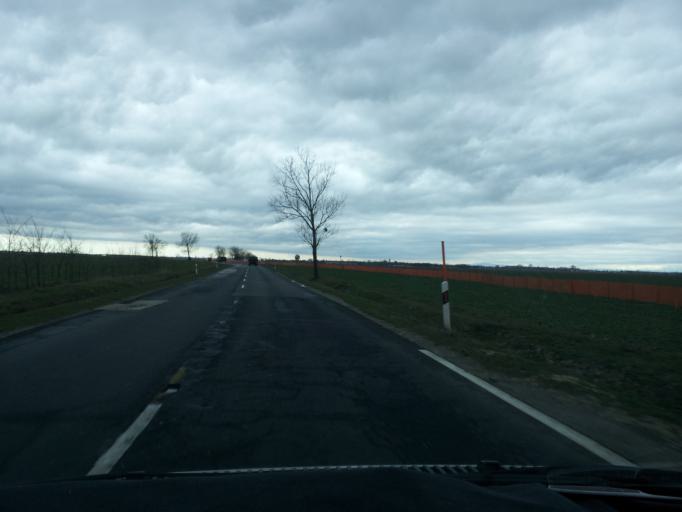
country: HU
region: Gyor-Moson-Sopron
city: Beled
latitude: 47.4765
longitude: 17.1367
